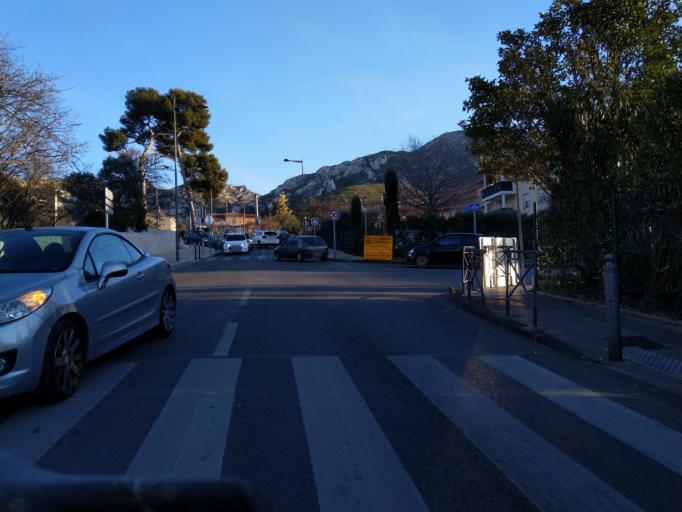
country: FR
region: Provence-Alpes-Cote d'Azur
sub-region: Departement des Bouches-du-Rhone
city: Marseille 11
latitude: 43.2743
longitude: 5.4349
